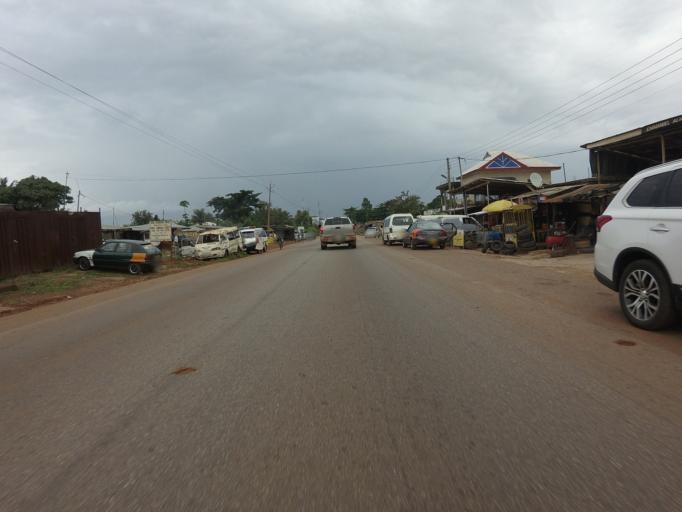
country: GH
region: Ashanti
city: Konongo
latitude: 6.6215
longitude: -1.1979
